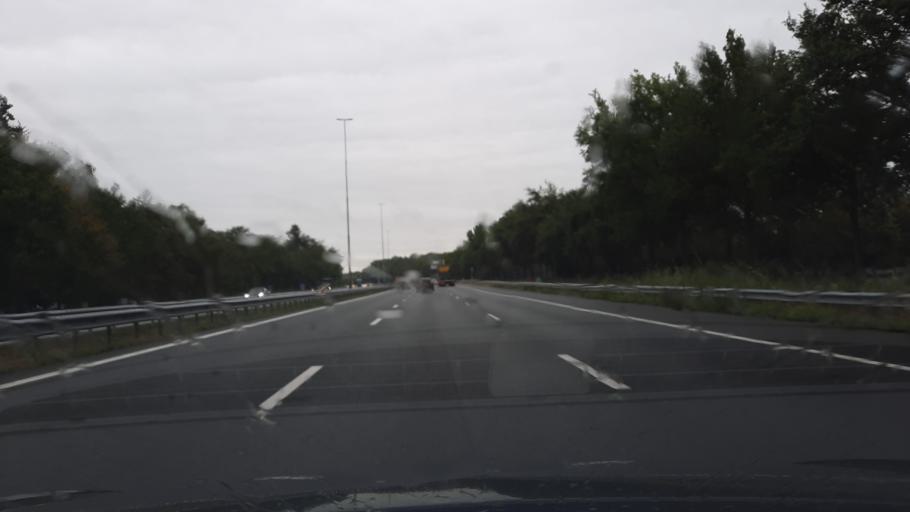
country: NL
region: North Brabant
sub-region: Gemeente Vught
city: Vught
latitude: 51.6376
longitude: 5.3124
